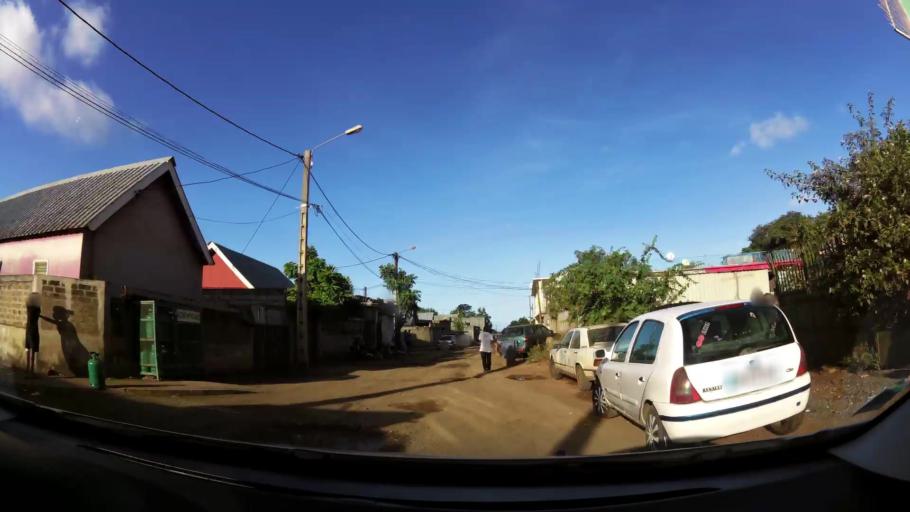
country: YT
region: Mamoudzou
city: Mamoudzou
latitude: -12.7961
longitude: 45.2136
